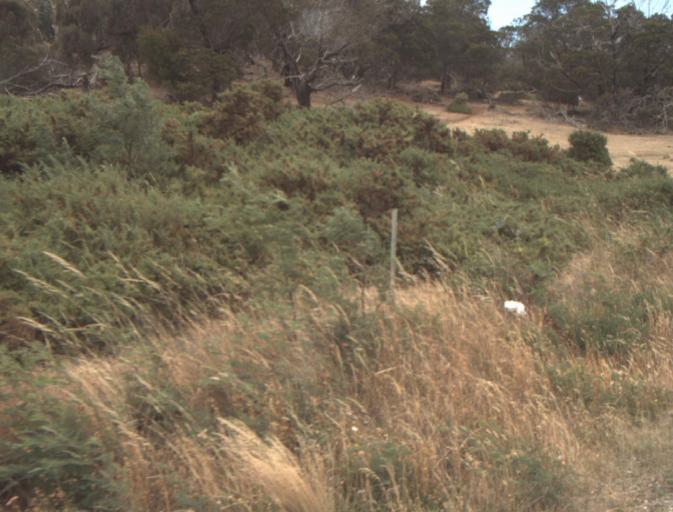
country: AU
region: Tasmania
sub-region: Northern Midlands
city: Evandale
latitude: -41.5128
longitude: 147.3077
